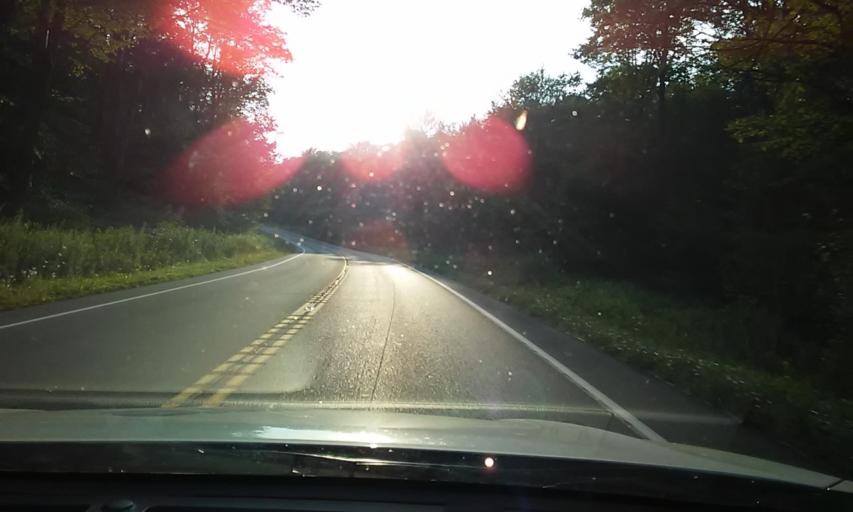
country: US
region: Pennsylvania
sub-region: McKean County
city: Kane
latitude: 41.5809
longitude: -78.9377
